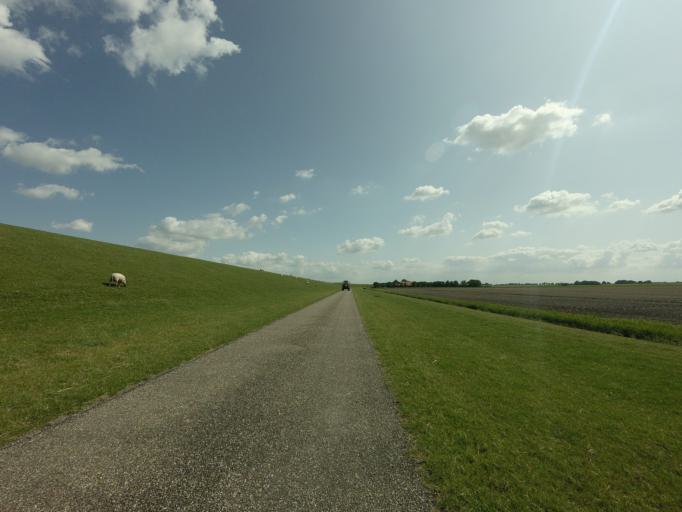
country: NL
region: Friesland
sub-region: Gemeente Ferwerderadiel
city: Hallum
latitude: 53.3241
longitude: 5.7334
